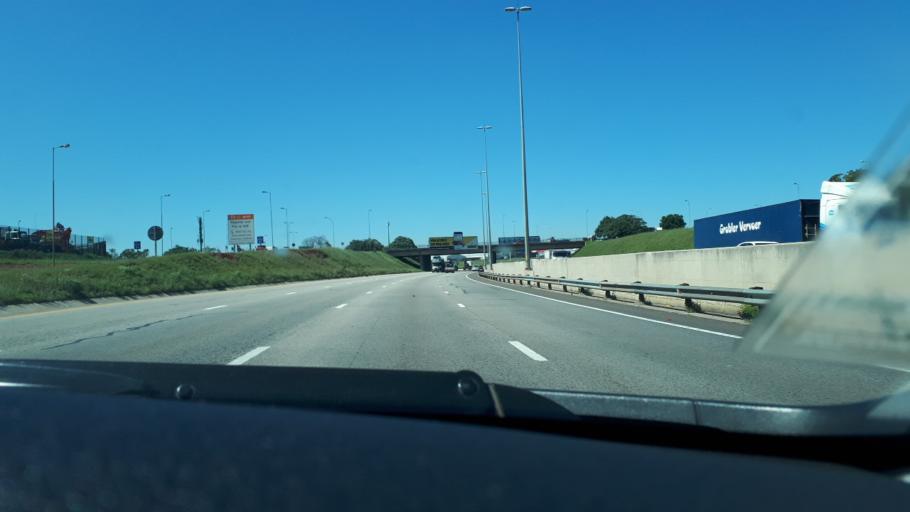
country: ZA
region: Gauteng
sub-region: Ekurhuleni Metropolitan Municipality
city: Tembisa
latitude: -26.0898
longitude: 28.2691
